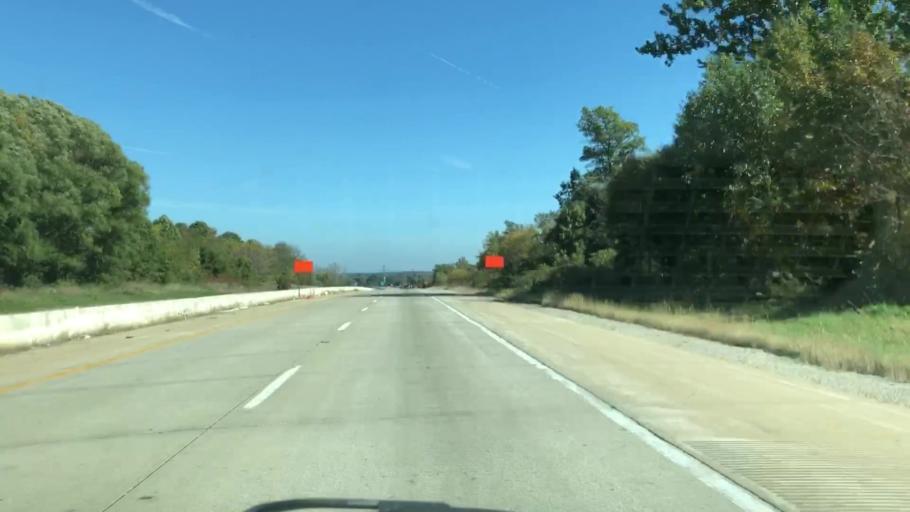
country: US
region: Indiana
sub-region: Elkhart County
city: Elkhart
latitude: 41.6378
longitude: -85.9759
